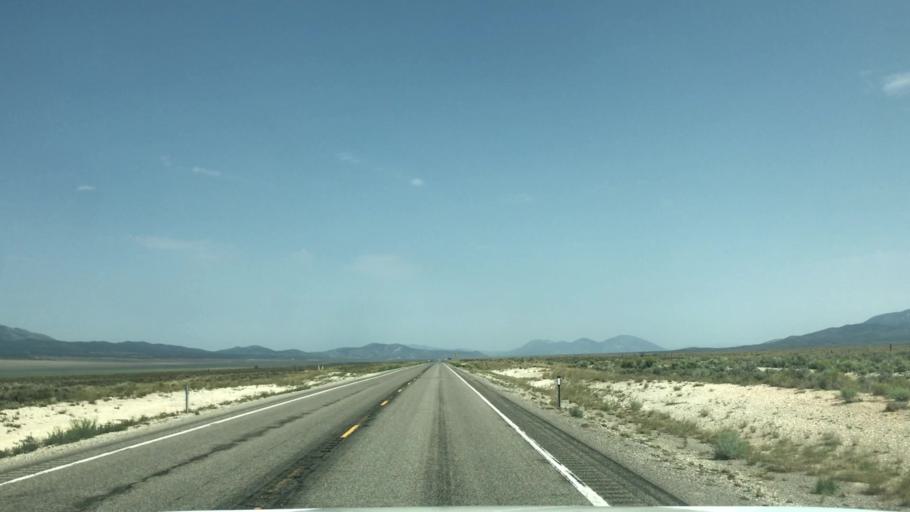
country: US
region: Nevada
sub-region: White Pine County
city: Ely
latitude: 39.0787
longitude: -114.7449
